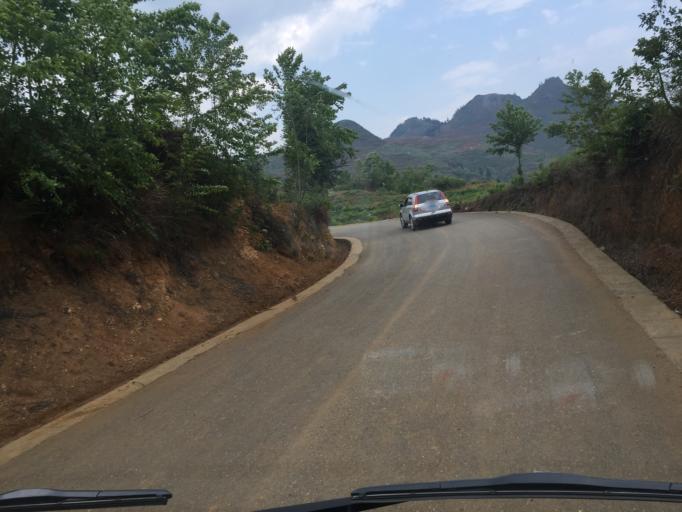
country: CN
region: Guangxi Zhuangzu Zizhiqu
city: Xinzhou
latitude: 25.6626
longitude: 105.2357
